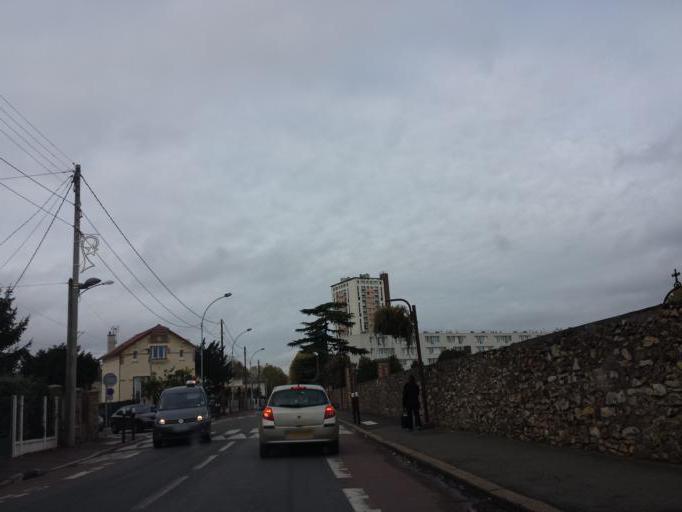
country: FR
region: Ile-de-France
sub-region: Departement du Val-d'Oise
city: Ermont
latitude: 48.9945
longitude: 2.2566
